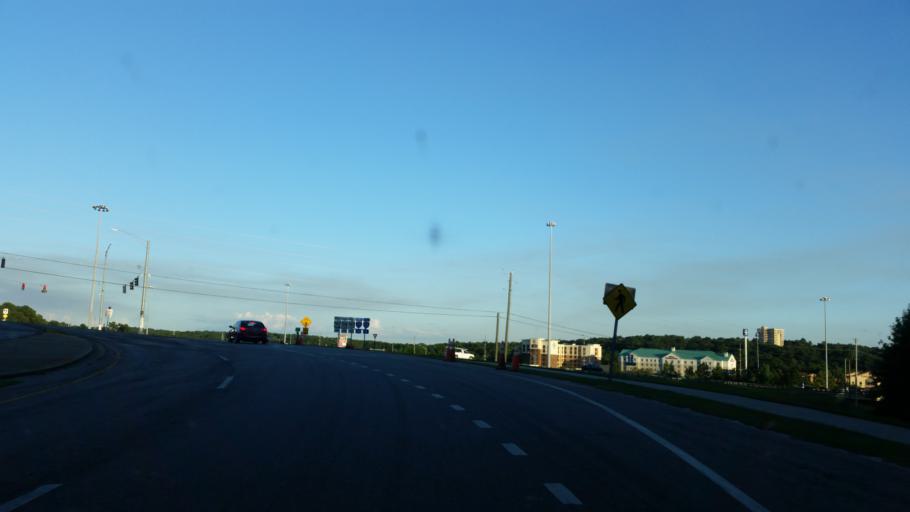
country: US
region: Alabama
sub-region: Baldwin County
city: Spanish Fort
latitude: 30.6580
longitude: -87.9127
